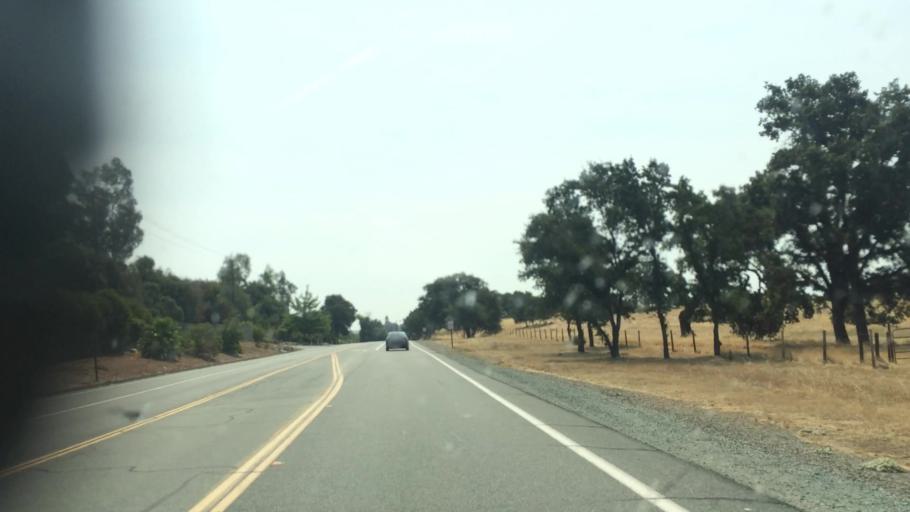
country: US
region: California
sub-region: Amador County
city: Ione
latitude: 38.3680
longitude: -120.9576
